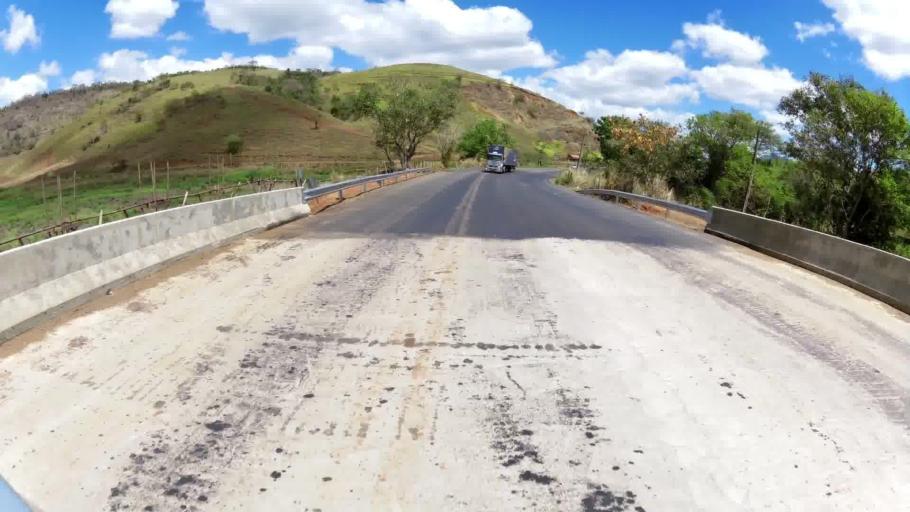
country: BR
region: Rio de Janeiro
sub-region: Itaperuna
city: Itaperuna
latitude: -21.3617
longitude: -41.9262
